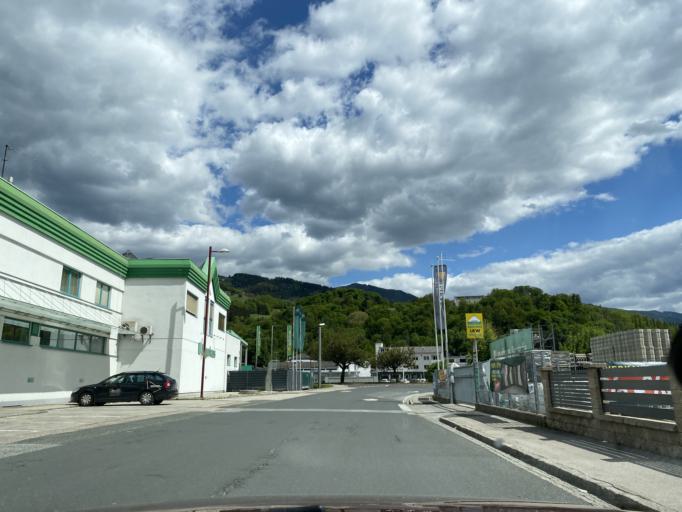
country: AT
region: Carinthia
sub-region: Politischer Bezirk Wolfsberg
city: Wolfsberg
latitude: 46.8436
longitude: 14.8401
